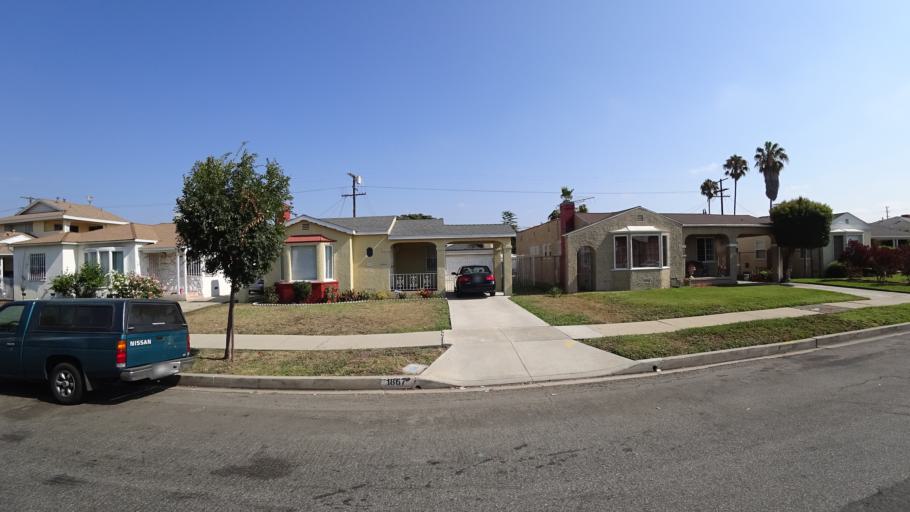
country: US
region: California
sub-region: Los Angeles County
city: Westmont
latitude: 33.9512
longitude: -118.3108
